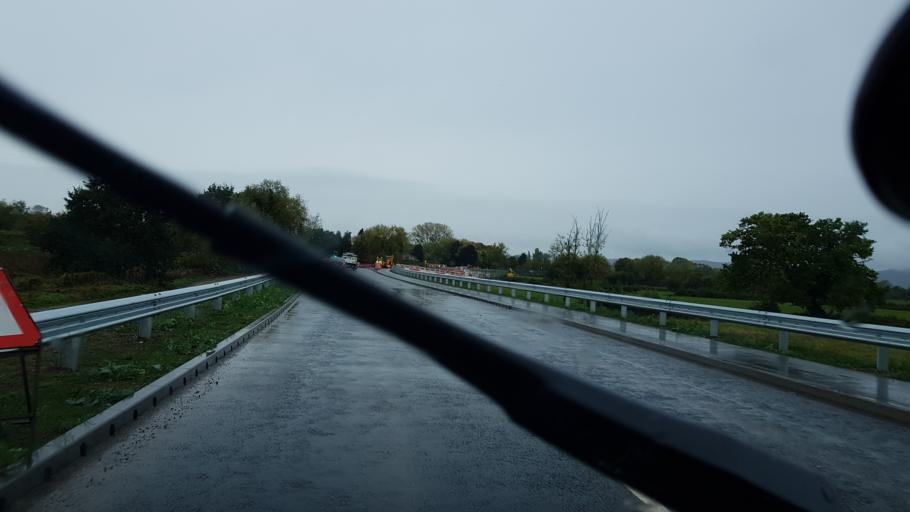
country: GB
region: England
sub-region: Worcestershire
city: Upton upon Severn
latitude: 52.0676
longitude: -2.2087
